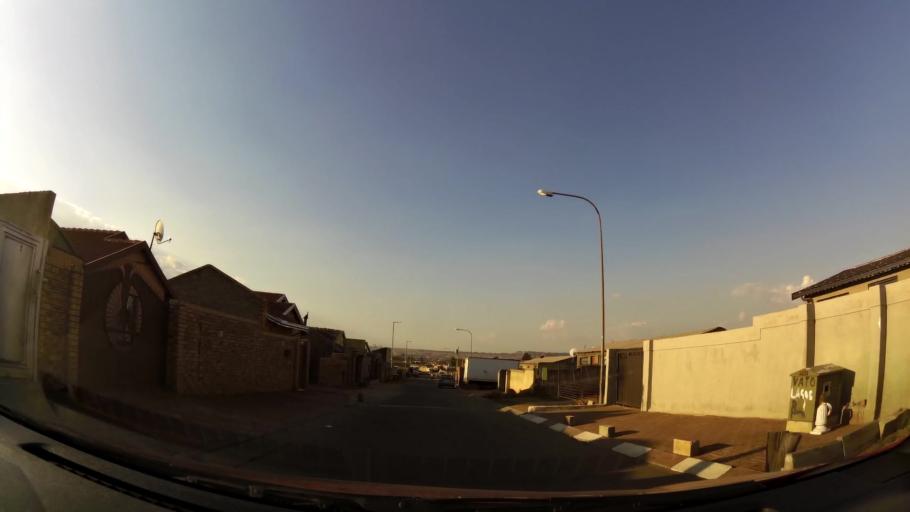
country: ZA
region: Gauteng
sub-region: City of Johannesburg Metropolitan Municipality
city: Soweto
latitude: -26.2305
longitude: 27.8564
